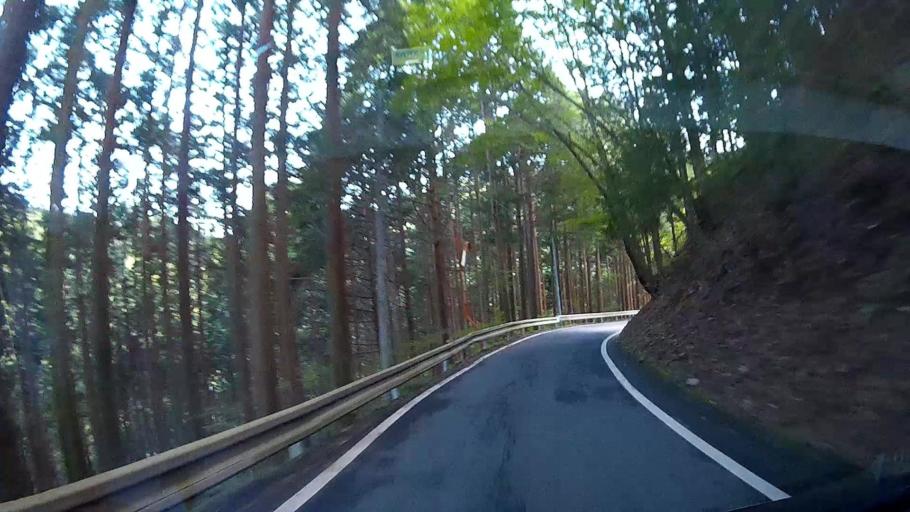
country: JP
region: Shizuoka
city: Shizuoka-shi
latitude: 35.1570
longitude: 138.2568
